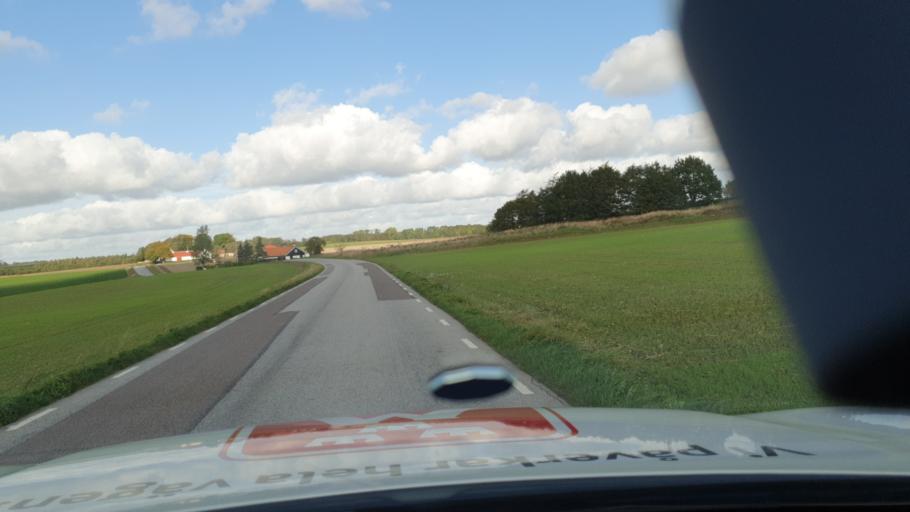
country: SE
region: Skane
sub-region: Ystads Kommun
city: Kopingebro
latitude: 55.4658
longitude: 14.0076
